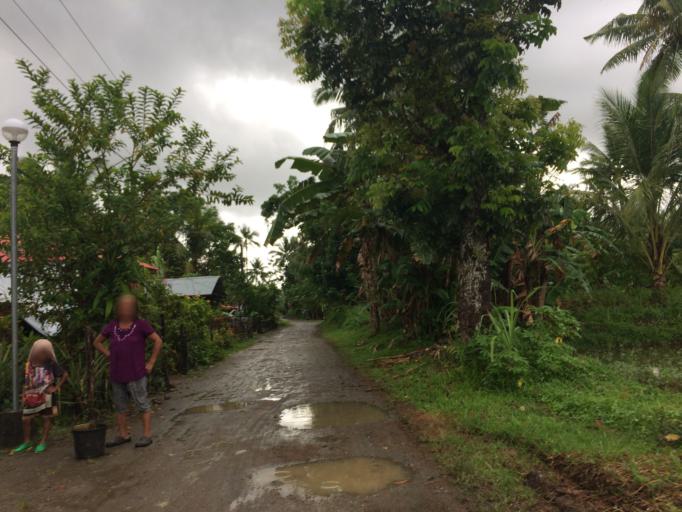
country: PH
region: Eastern Visayas
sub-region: Province of Leyte
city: Bugho
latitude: 10.8020
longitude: 124.9705
